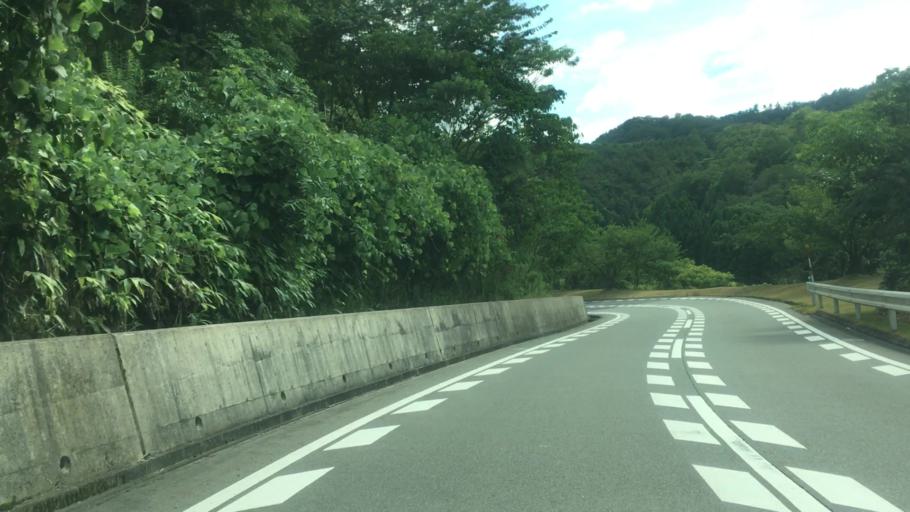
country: JP
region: Hyogo
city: Toyooka
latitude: 35.5226
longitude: 134.7910
